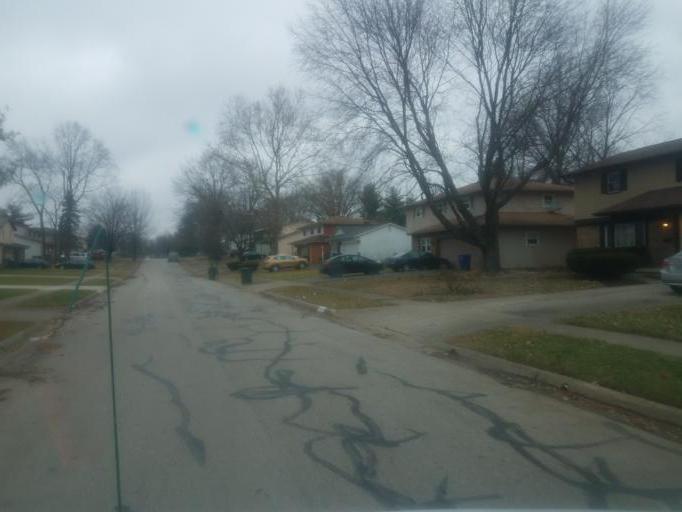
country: US
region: Ohio
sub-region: Franklin County
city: Minerva Park
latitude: 40.0777
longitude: -82.9717
